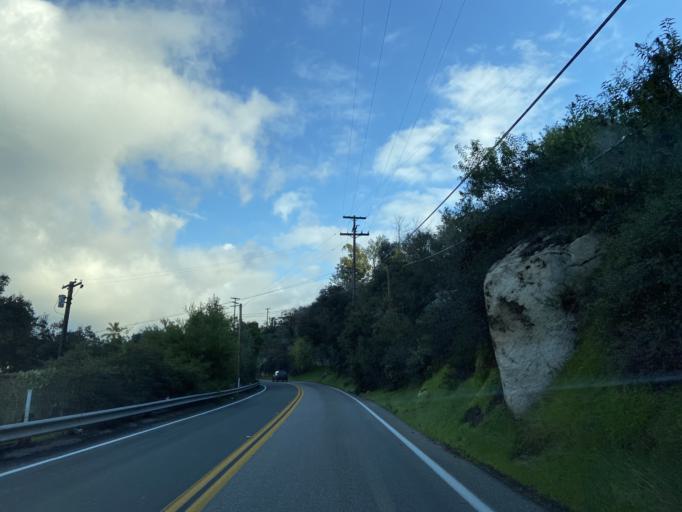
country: US
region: California
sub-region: San Diego County
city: Casa de Oro-Mount Helix
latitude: 32.7757
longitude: -116.9882
